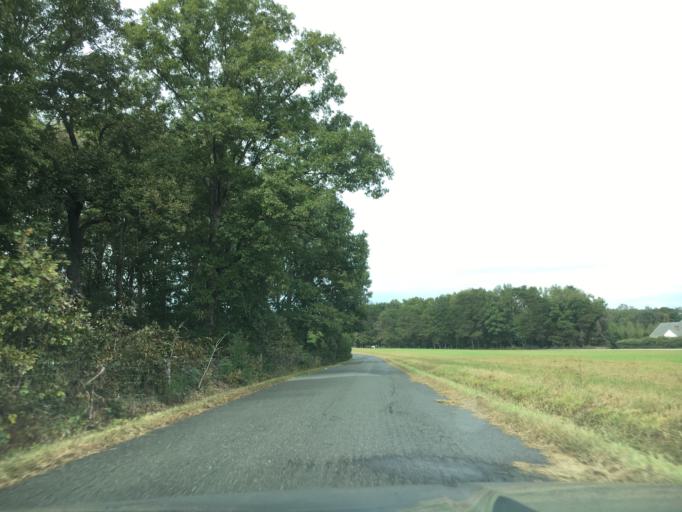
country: US
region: Virginia
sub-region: Goochland County
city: Goochland
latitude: 37.7084
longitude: -77.8404
